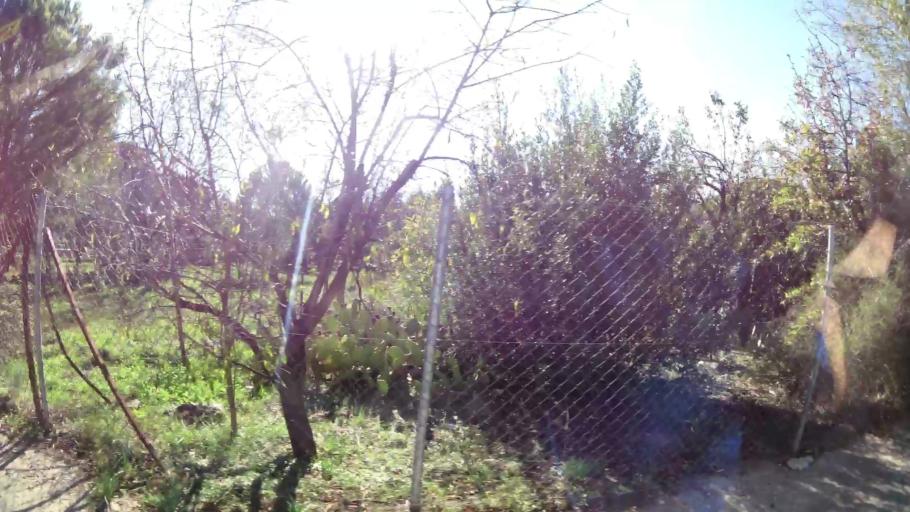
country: GR
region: Attica
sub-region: Nomarchia Athinas
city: Nea Erythraia
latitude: 38.1061
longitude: 23.8205
